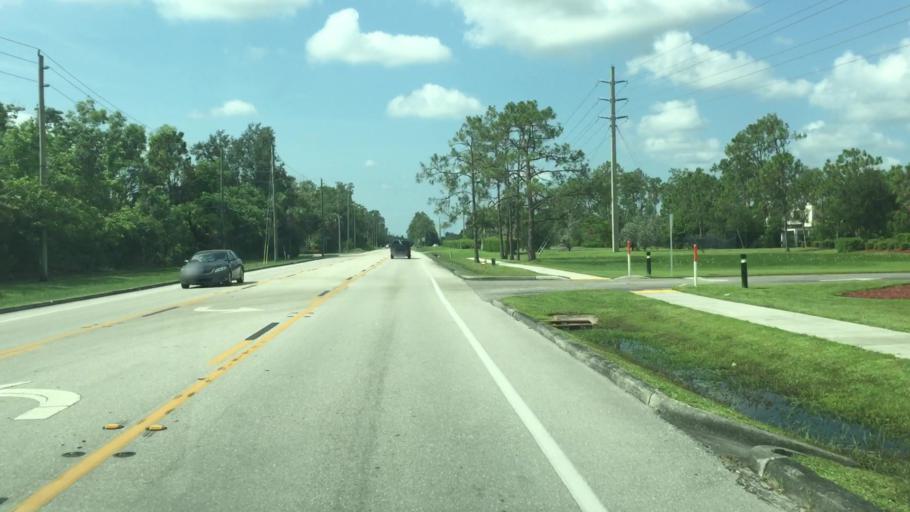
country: US
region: Florida
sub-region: Lee County
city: Villas
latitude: 26.5620
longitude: -81.8470
